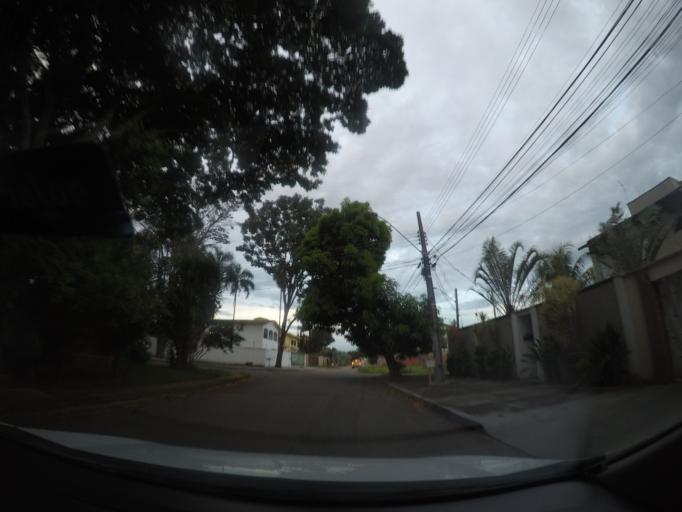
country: BR
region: Goias
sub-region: Goiania
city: Goiania
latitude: -16.6484
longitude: -49.2253
